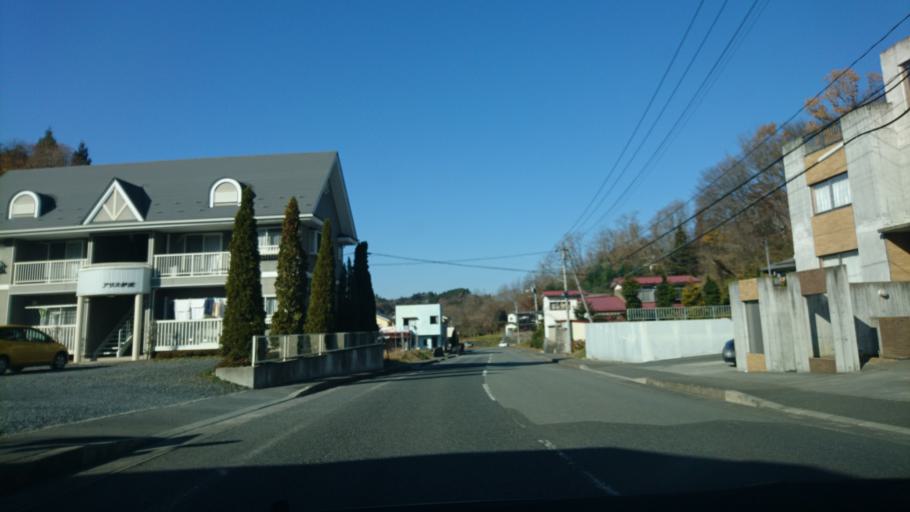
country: JP
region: Iwate
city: Ichinoseki
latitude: 38.9162
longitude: 141.3419
